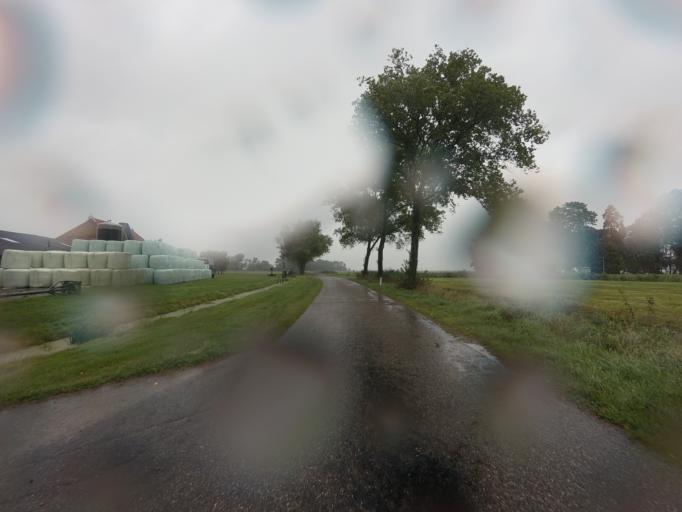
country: NL
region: Friesland
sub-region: Gemeente Boarnsterhim
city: Aldeboarn
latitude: 53.0710
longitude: 5.9288
